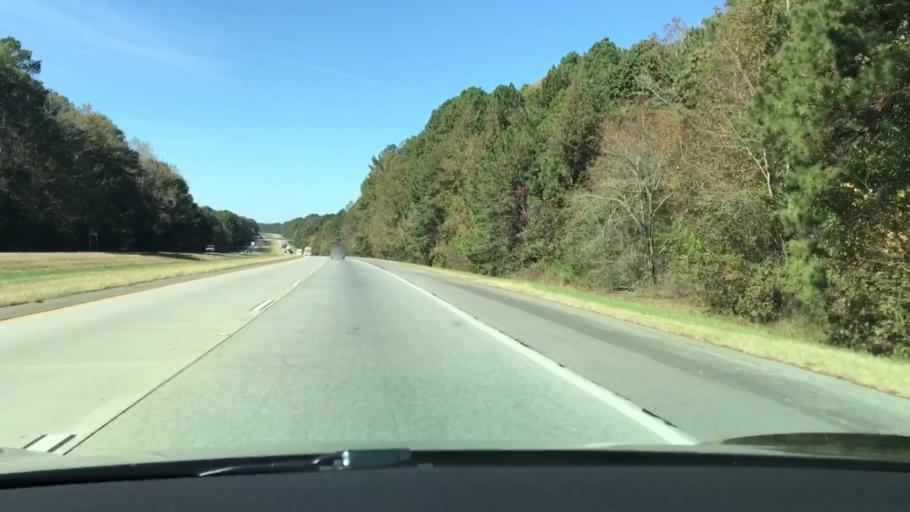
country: US
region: Georgia
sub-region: Greene County
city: Union Point
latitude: 33.5467
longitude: -83.0332
